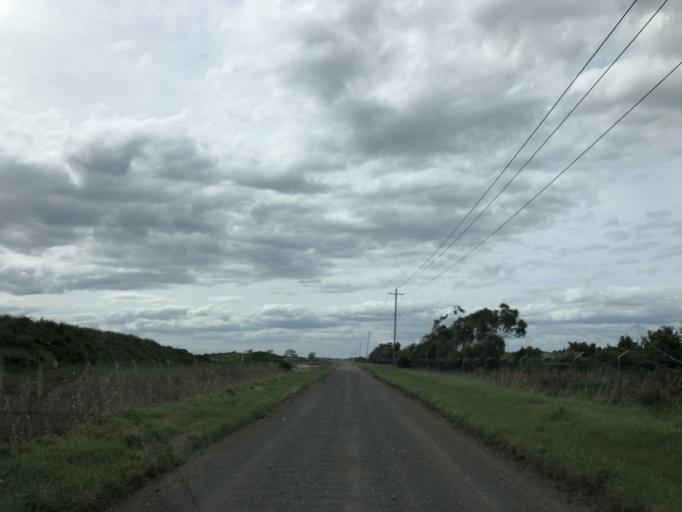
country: AU
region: Victoria
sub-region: Kingston
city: Patterson Lakes
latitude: -38.0751
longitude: 145.1658
